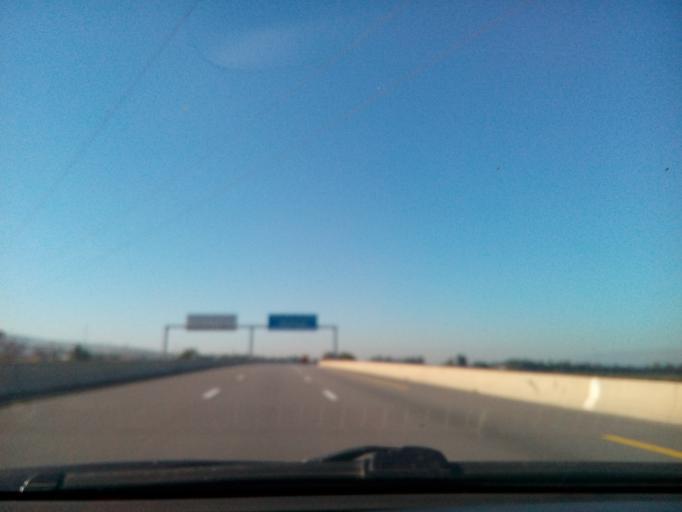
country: DZ
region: Chlef
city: Boukadir
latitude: 36.0239
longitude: 1.0552
